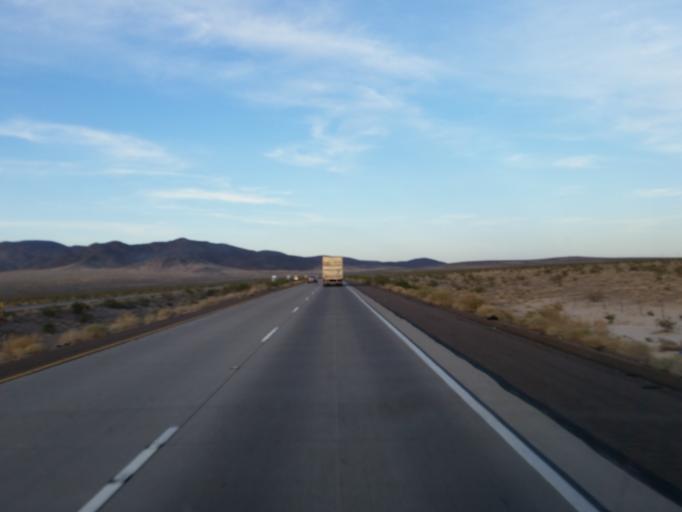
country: US
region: California
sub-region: San Bernardino County
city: Twentynine Palms
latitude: 34.7266
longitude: -116.1255
